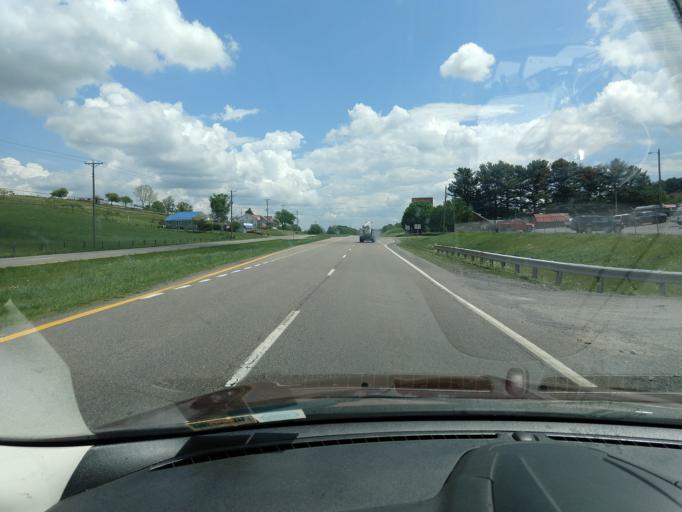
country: US
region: Virginia
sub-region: Russell County
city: Honaker
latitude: 36.9738
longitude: -81.8909
